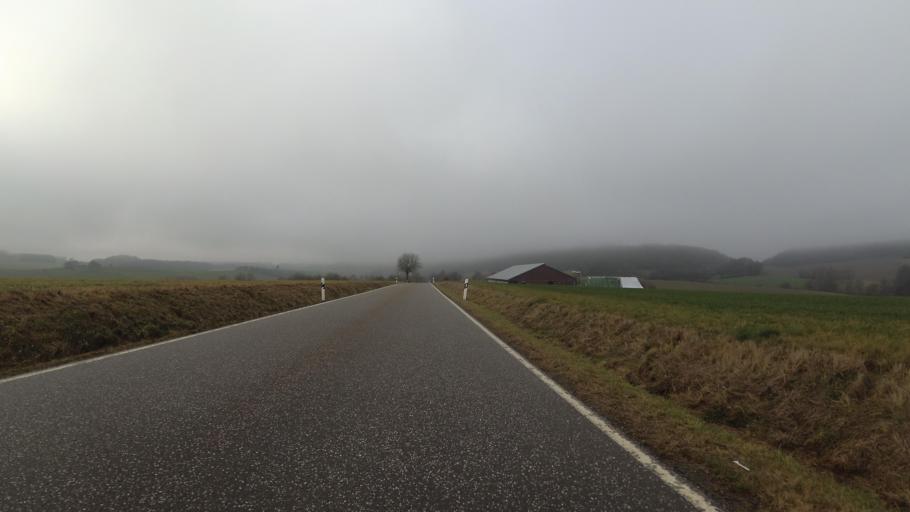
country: DE
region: Rheinland-Pfalz
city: Konken
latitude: 49.5197
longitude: 7.3437
